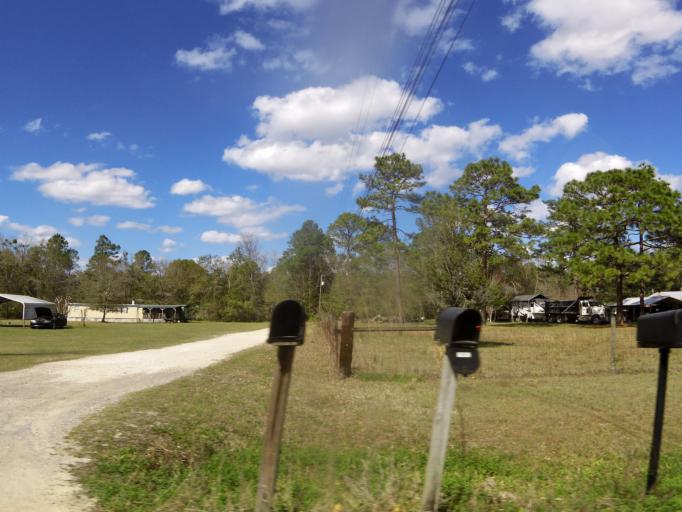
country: US
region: Florida
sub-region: Clay County
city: Middleburg
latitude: 30.1169
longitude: -81.9522
